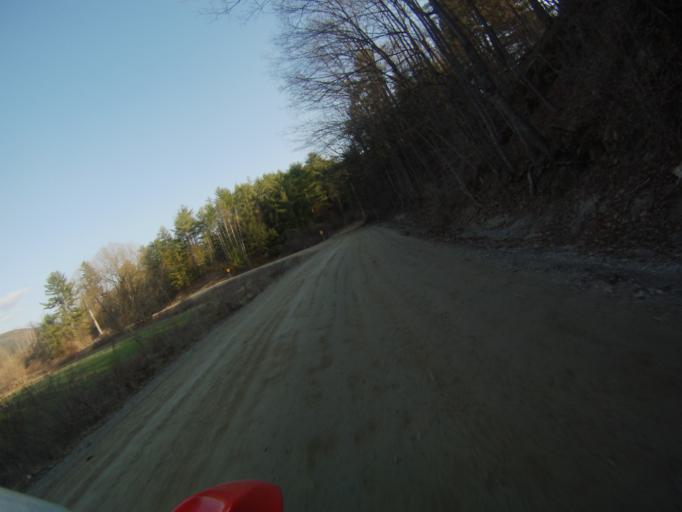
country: US
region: Vermont
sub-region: Addison County
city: Bristol
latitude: 44.0915
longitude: -73.1035
